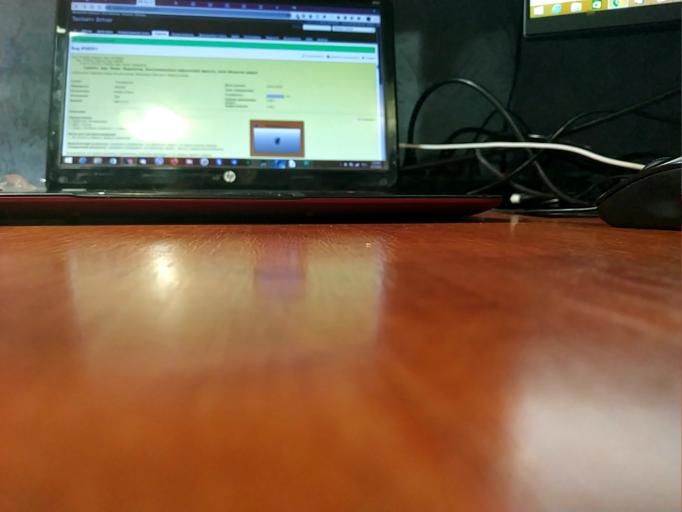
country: RU
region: Vologda
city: Kaduy
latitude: 59.4614
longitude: 37.3305
